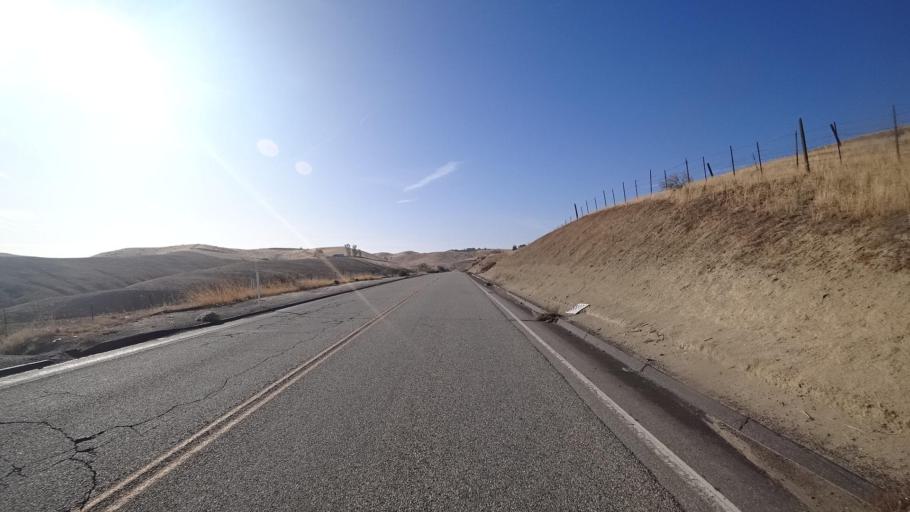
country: US
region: California
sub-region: Kern County
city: Oildale
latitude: 35.5183
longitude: -118.9798
